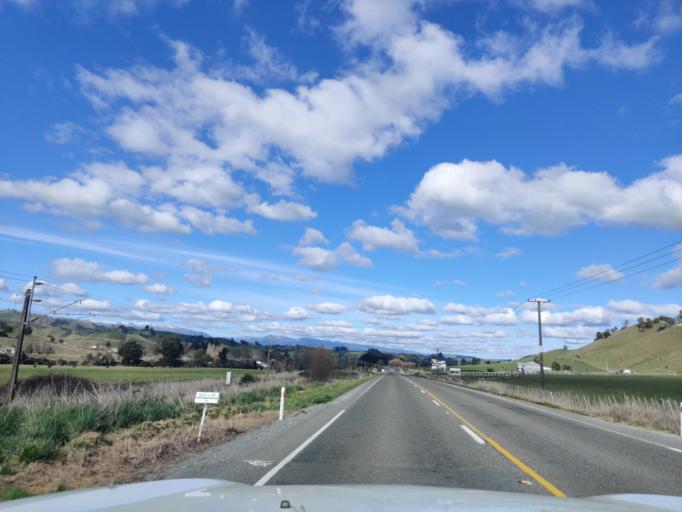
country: NZ
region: Manawatu-Wanganui
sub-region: Ruapehu District
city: Waiouru
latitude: -39.7066
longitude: 175.8331
